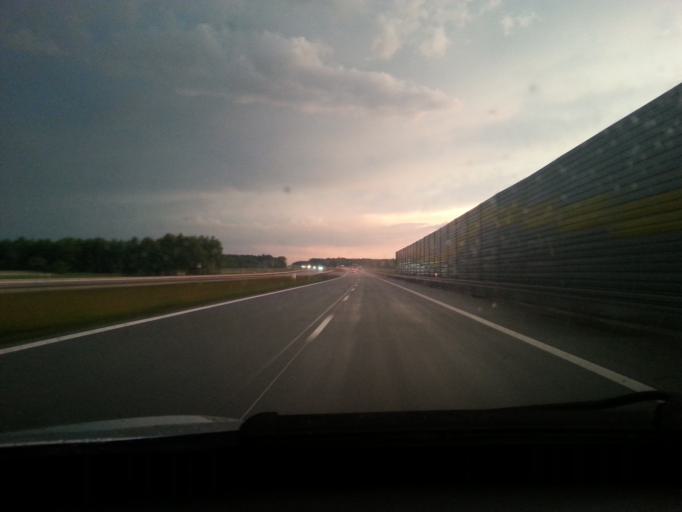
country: PL
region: Lodz Voivodeship
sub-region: Powiat pabianicki
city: Dobron
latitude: 51.5893
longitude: 19.2089
